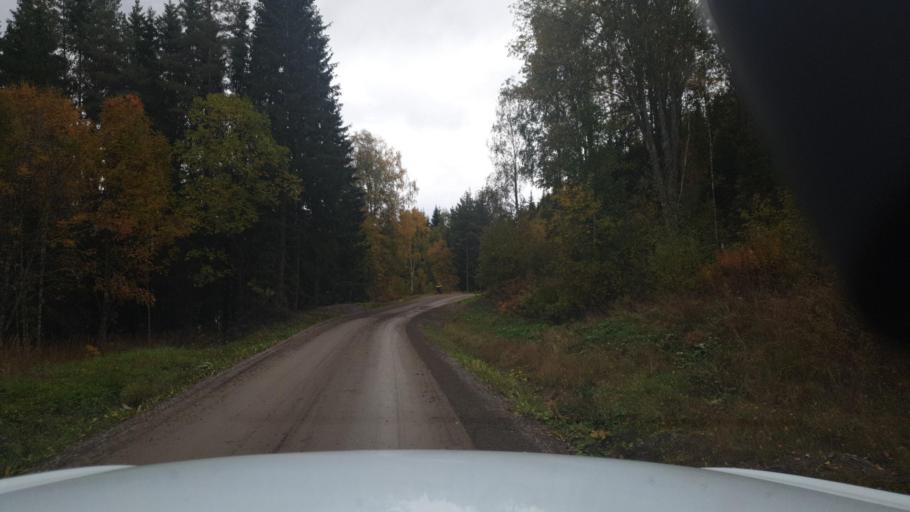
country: SE
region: Vaermland
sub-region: Eda Kommun
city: Charlottenberg
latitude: 60.0301
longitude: 12.6047
